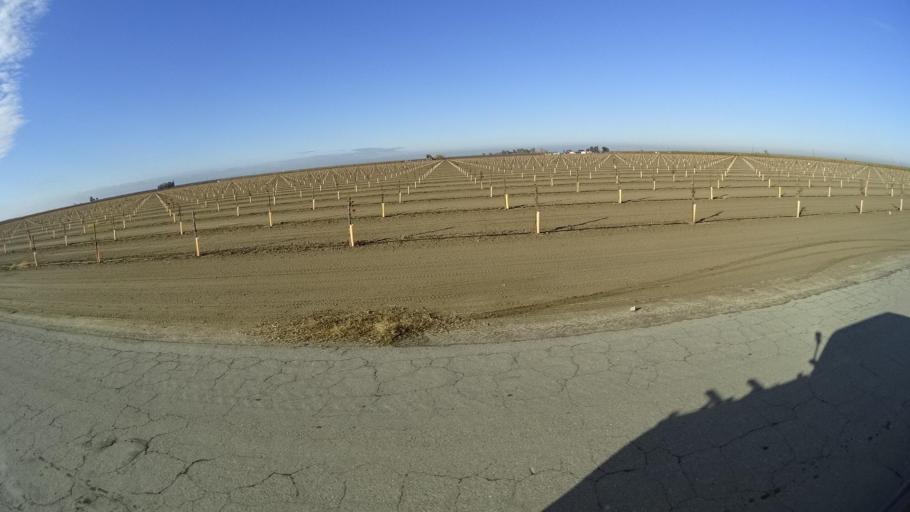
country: US
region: California
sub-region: Kern County
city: Delano
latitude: 35.7147
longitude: -119.3030
